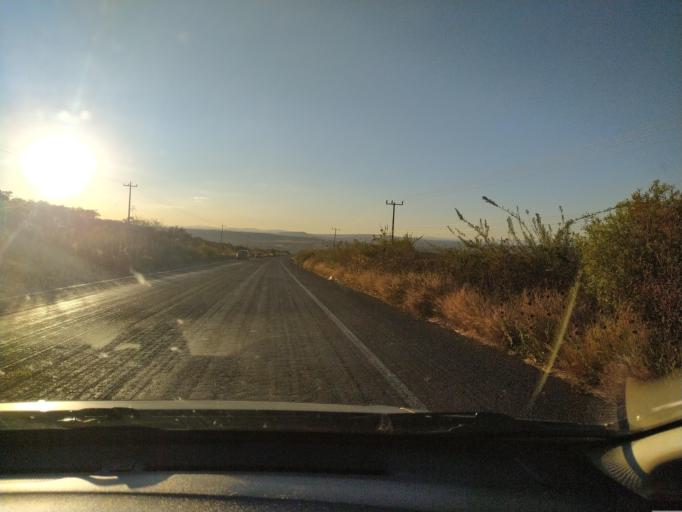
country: MX
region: Jalisco
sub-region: San Julian
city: Colonia Veintitres de Mayo
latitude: 21.0086
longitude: -102.2548
